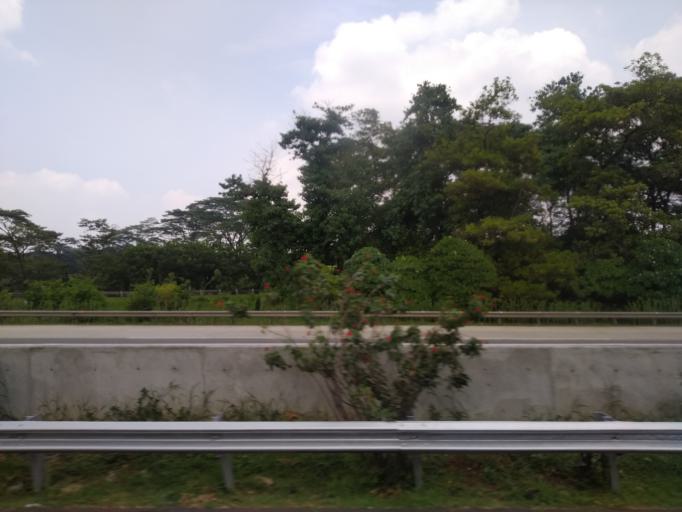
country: ID
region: West Java
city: Citeureup
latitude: -6.4565
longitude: 106.8873
